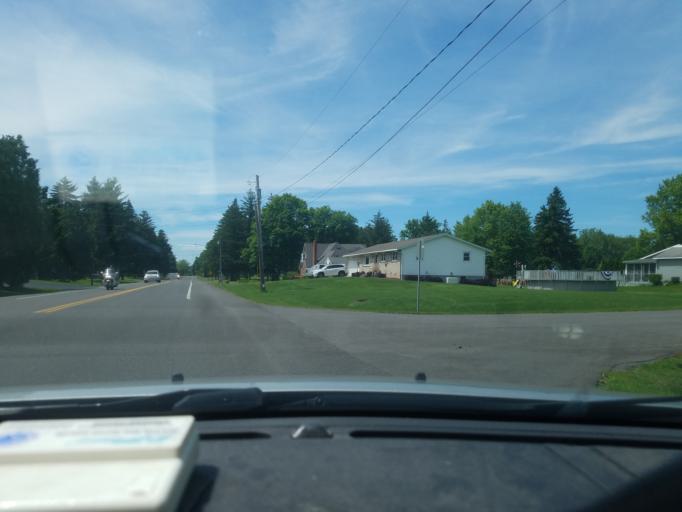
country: US
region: New York
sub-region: Onondaga County
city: East Syracuse
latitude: 43.0810
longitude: -76.0723
